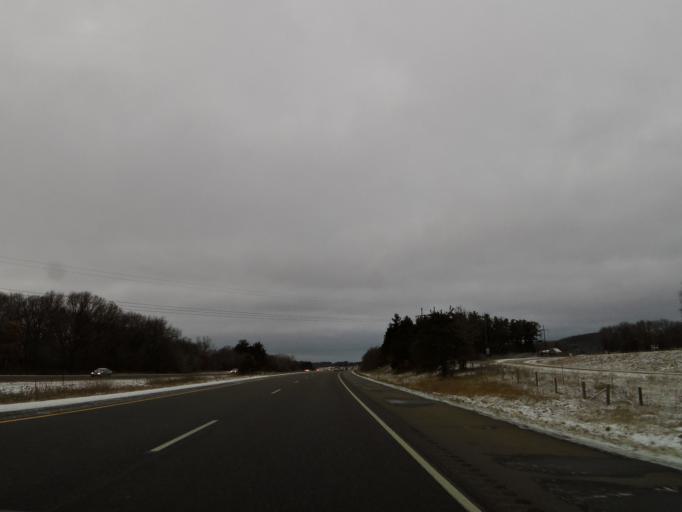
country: US
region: Wisconsin
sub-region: Eau Claire County
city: Fall Creek
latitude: 44.7311
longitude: -91.3657
